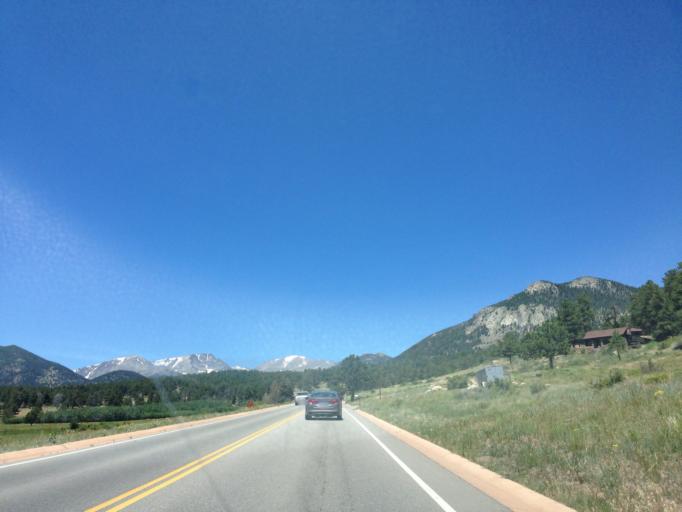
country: US
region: Colorado
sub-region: Larimer County
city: Estes Park
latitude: 40.3558
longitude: -105.5835
